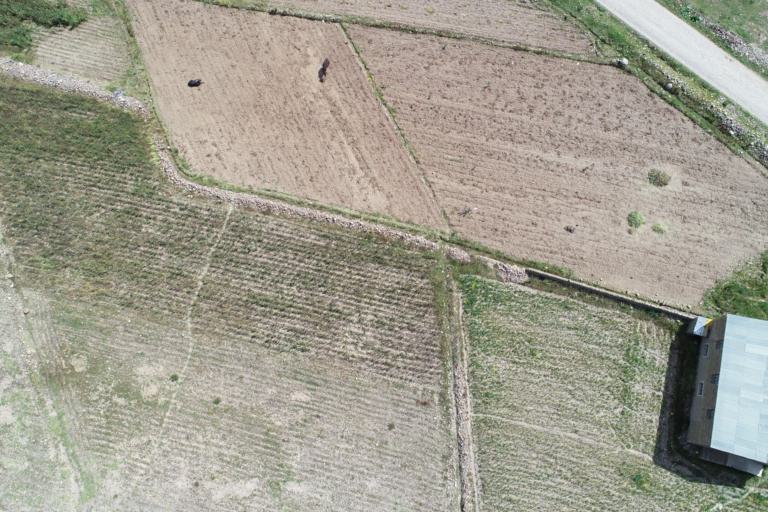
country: BO
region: La Paz
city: Achacachi
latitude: -16.0219
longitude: -68.6161
